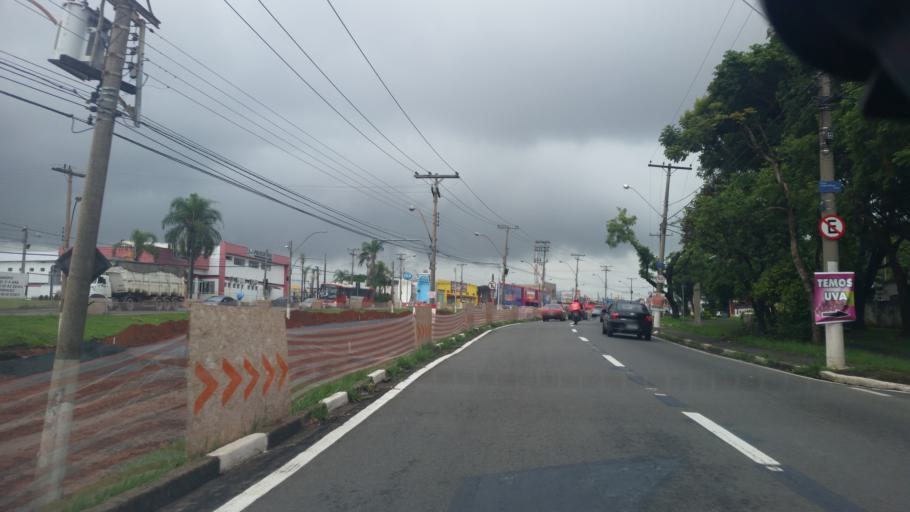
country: BR
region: Sao Paulo
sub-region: Campinas
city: Campinas
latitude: -22.9176
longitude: -47.1061
